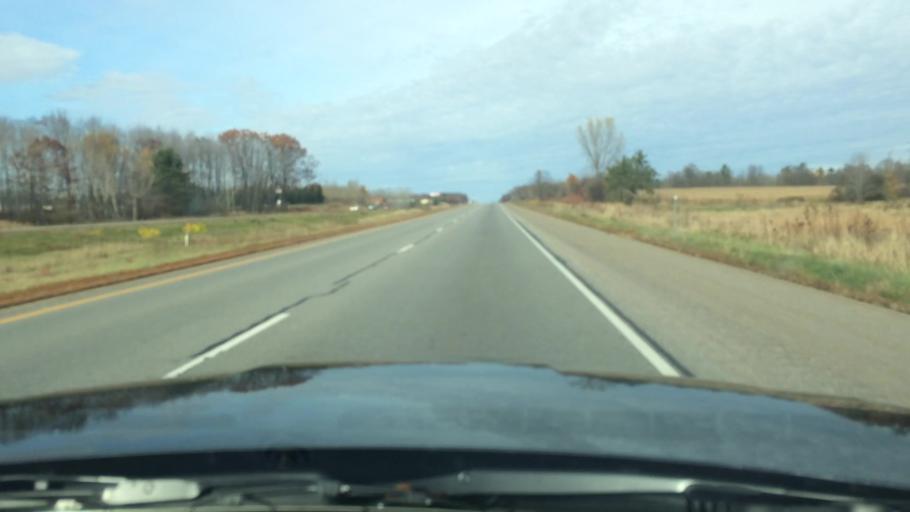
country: US
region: Wisconsin
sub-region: Marathon County
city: Mosinee
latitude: 44.7487
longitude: -89.6797
